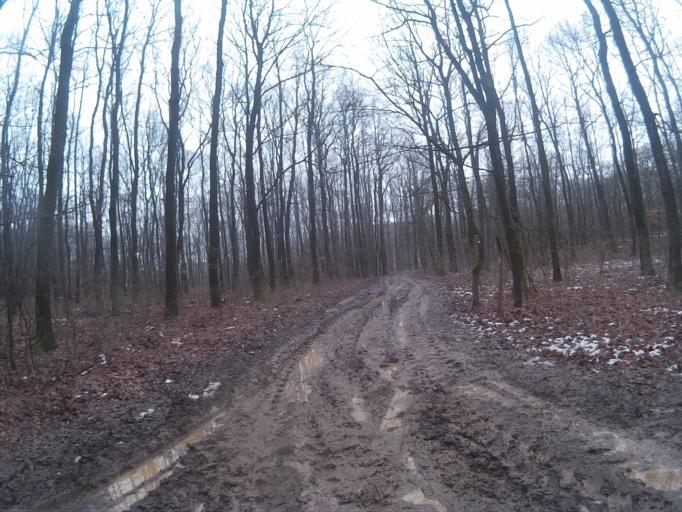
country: HU
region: Komarom-Esztergom
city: Tardos
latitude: 47.6456
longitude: 18.4743
